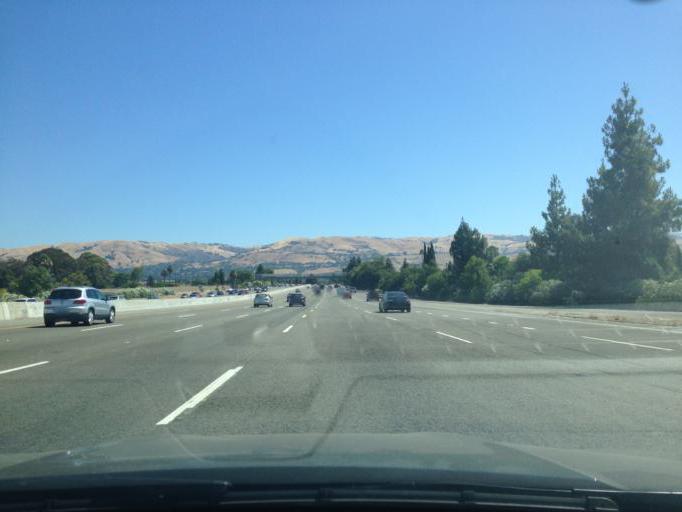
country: US
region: California
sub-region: Santa Clara County
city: Alum Rock
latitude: 37.3441
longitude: -121.8452
